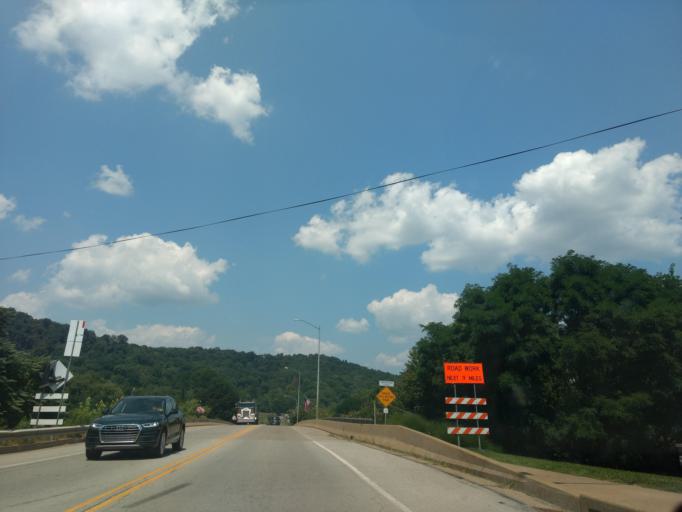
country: US
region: Pennsylvania
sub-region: Butler County
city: Zelienople
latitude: 40.7983
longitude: -80.1375
